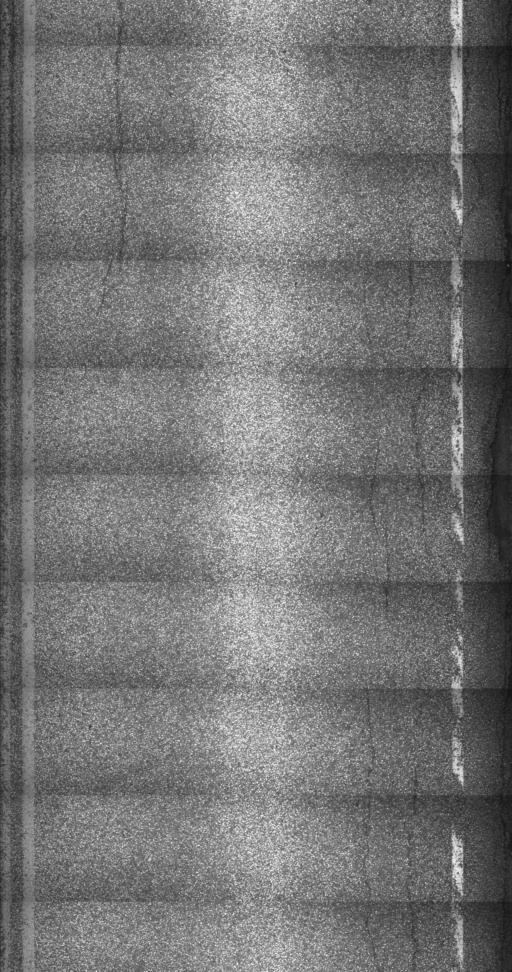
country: US
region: Vermont
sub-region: Lamoille County
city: Johnson
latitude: 44.5213
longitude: -72.7722
